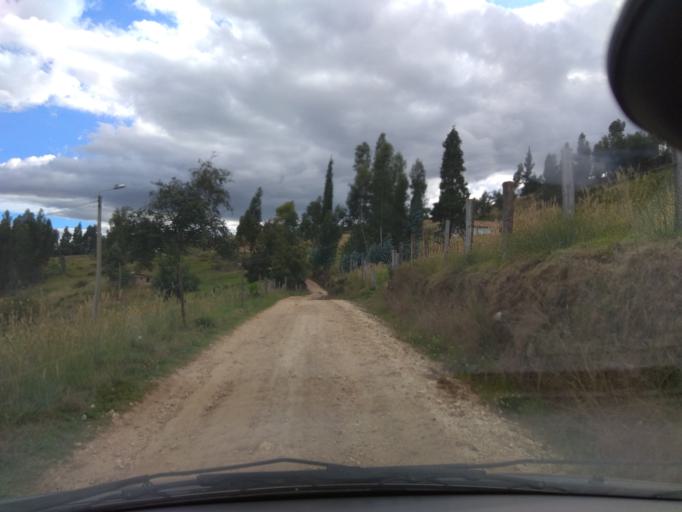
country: CO
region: Boyaca
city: Paipa
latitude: 5.8134
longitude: -73.0952
